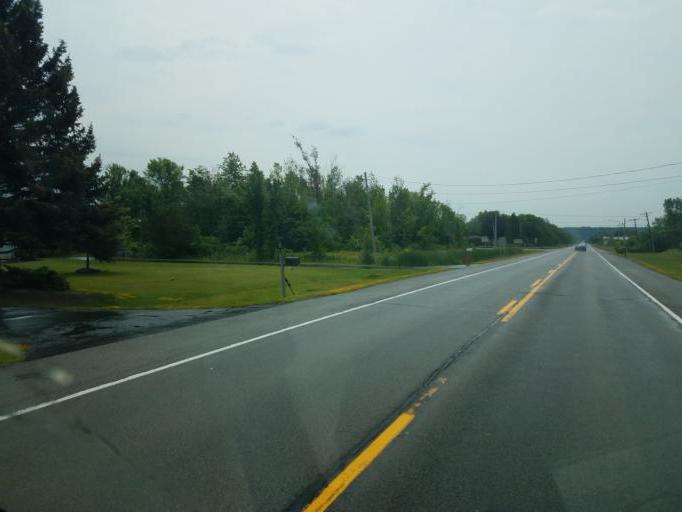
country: US
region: New York
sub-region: Niagara County
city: Lewiston
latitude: 43.1996
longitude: -79.0177
